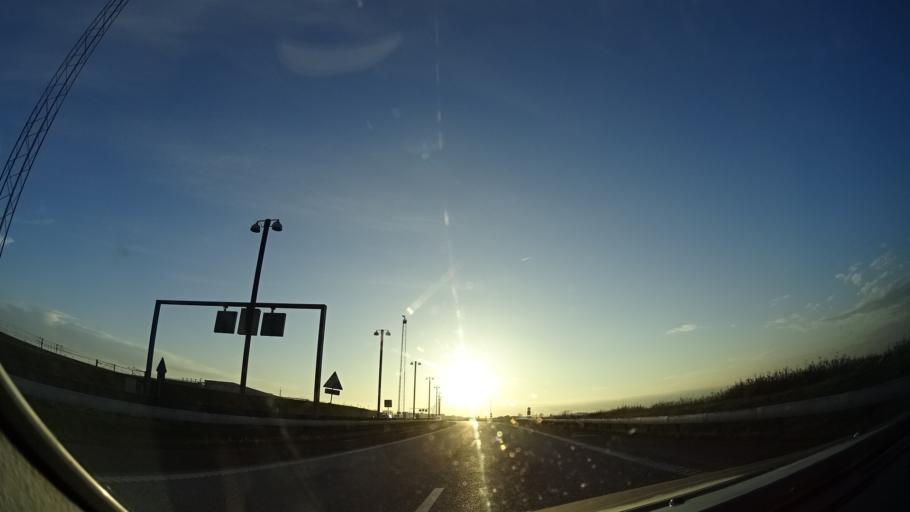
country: DK
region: Capital Region
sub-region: Dragor Kommune
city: Dragor
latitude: 55.6328
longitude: 12.6724
